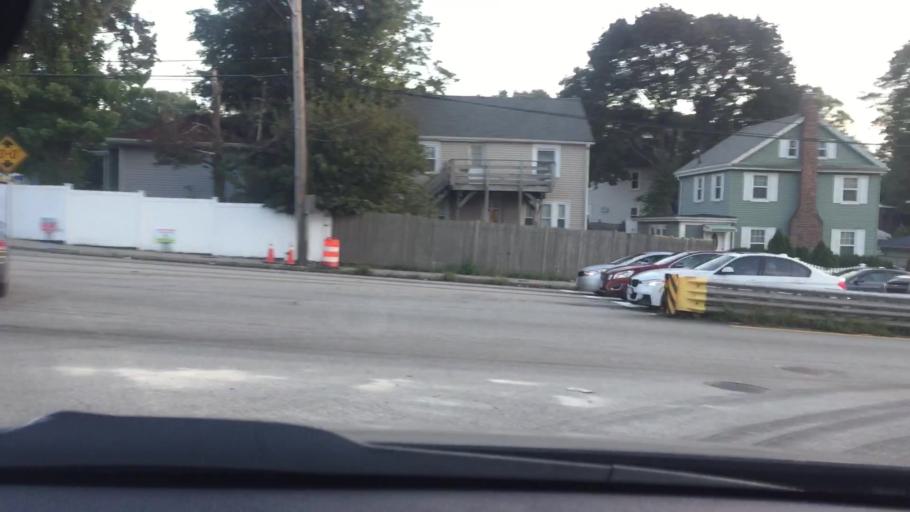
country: US
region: Massachusetts
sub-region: Middlesex County
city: Newton
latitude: 42.3190
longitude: -71.2128
